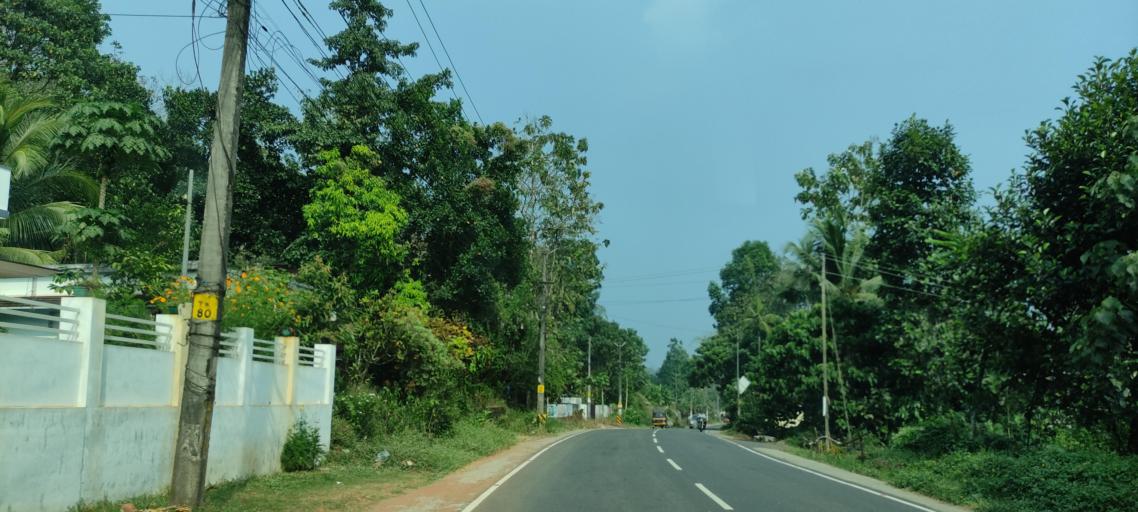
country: IN
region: Kerala
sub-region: Ernakulam
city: Piravam
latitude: 9.7937
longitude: 76.4633
